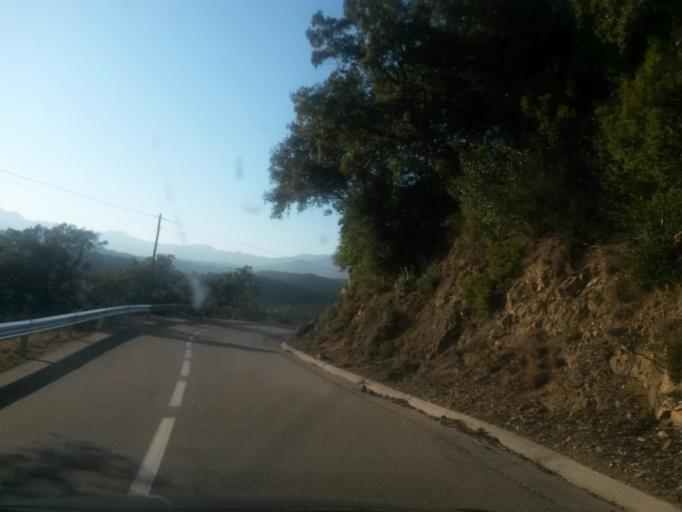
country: ES
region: Catalonia
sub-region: Provincia de Girona
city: Darnius
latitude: 42.3770
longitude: 2.7960
